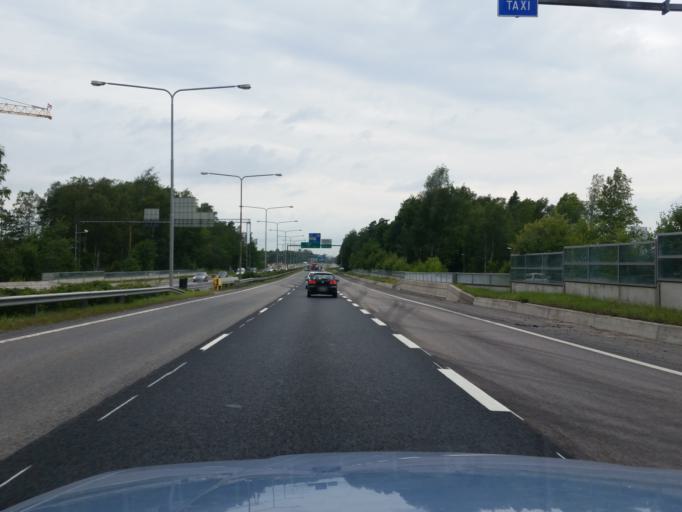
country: FI
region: Uusimaa
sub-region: Helsinki
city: Teekkarikylae
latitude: 60.1640
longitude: 24.8543
